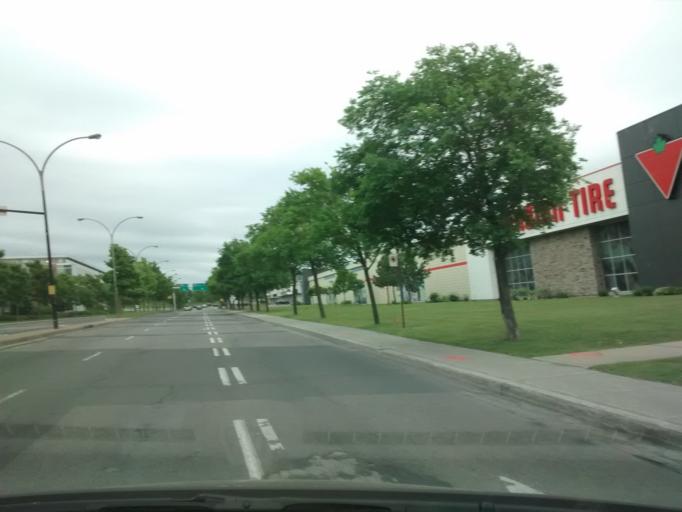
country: CA
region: Quebec
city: Mont-Royal
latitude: 45.5322
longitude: -73.6535
